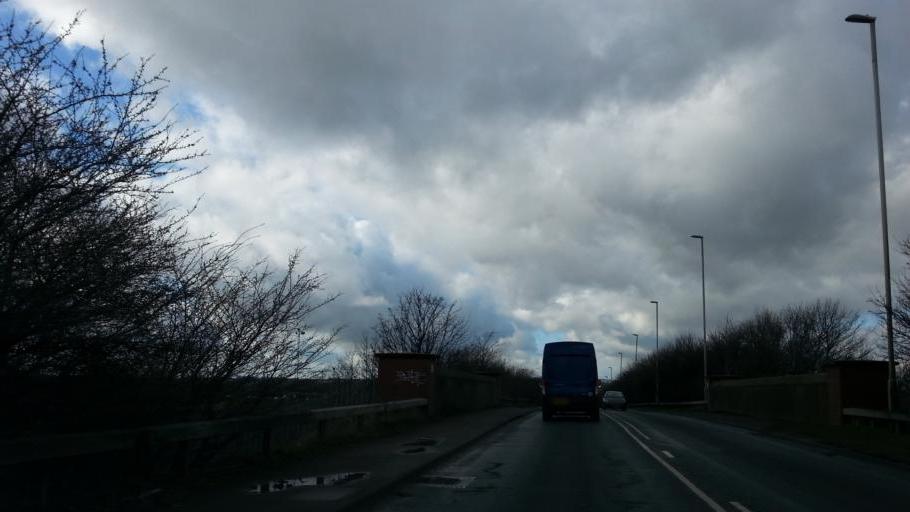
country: GB
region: England
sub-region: Leicestershire
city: Syston
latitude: 52.6636
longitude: -1.0935
